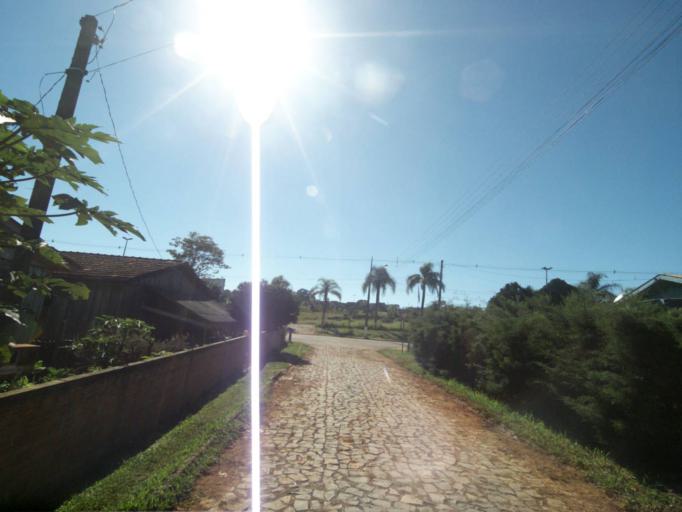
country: BR
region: Parana
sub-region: Pinhao
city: Pinhao
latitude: -25.8434
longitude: -52.0311
